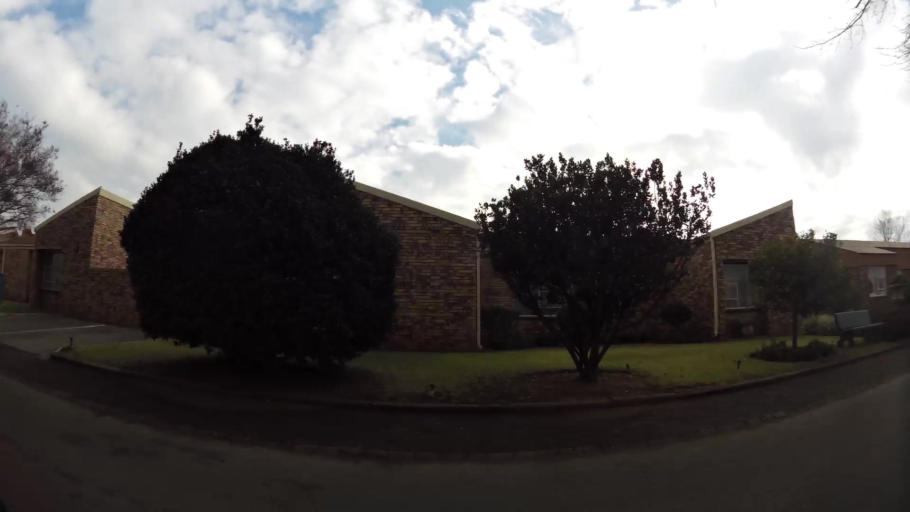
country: ZA
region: Gauteng
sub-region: Sedibeng District Municipality
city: Vanderbijlpark
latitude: -26.7056
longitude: 27.8298
